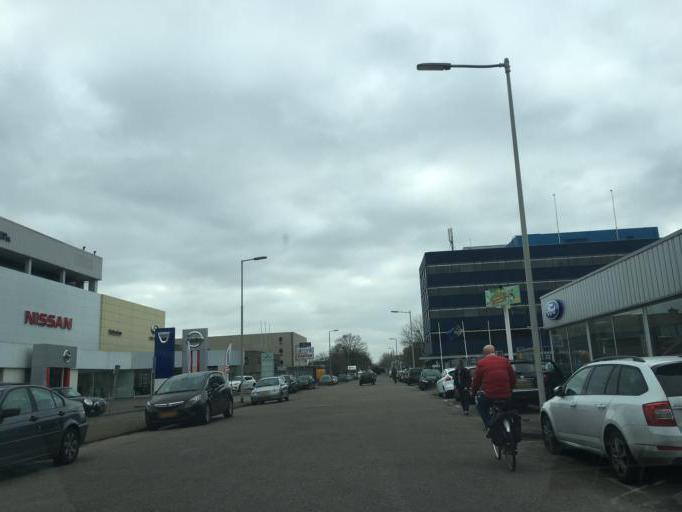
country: NL
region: South Holland
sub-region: Gemeente Rotterdam
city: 's-Gravenland
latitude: 51.9499
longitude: 4.5499
